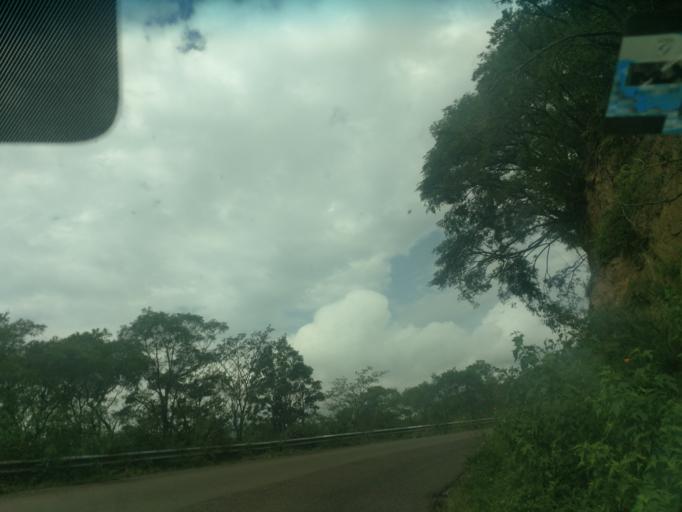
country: MX
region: Jalisco
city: El Salto
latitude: 20.3679
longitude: -104.5896
